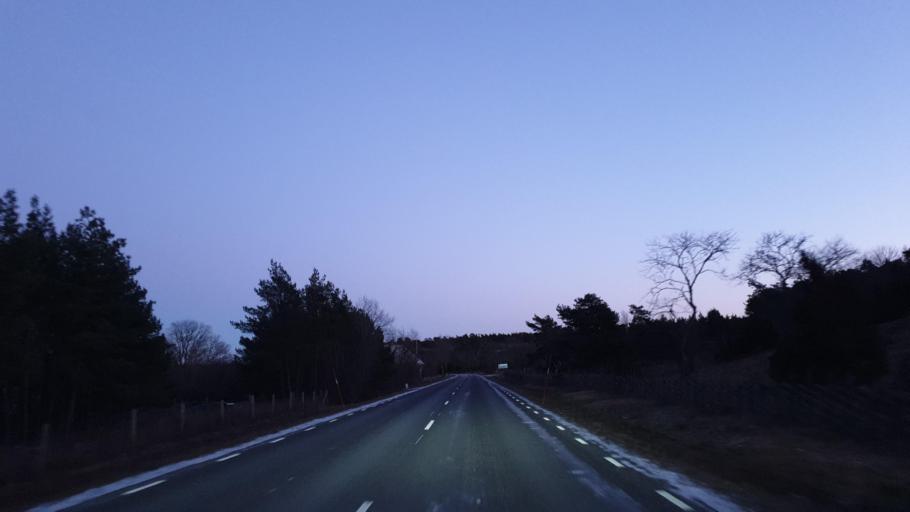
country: SE
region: Gotland
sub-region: Gotland
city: Slite
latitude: 57.4234
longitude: 18.8477
